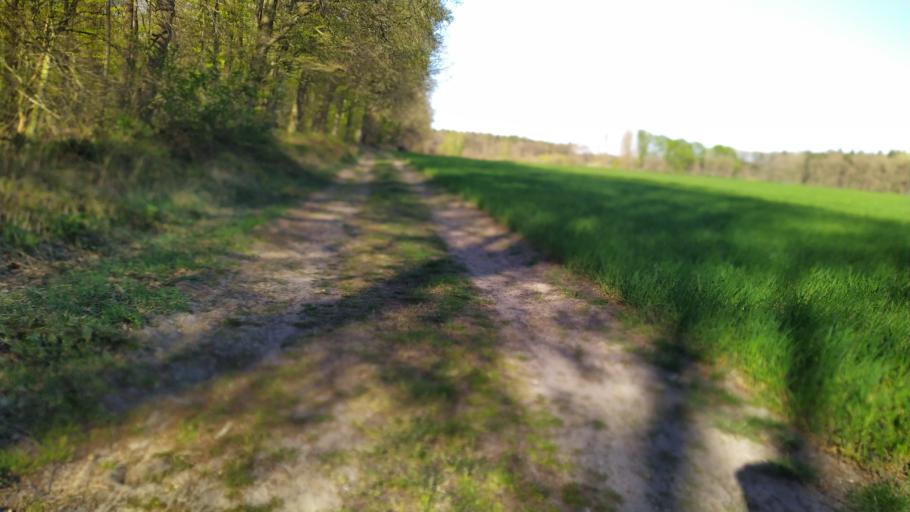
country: DE
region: Lower Saxony
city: Klein Meckelsen
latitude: 53.2968
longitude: 9.4297
